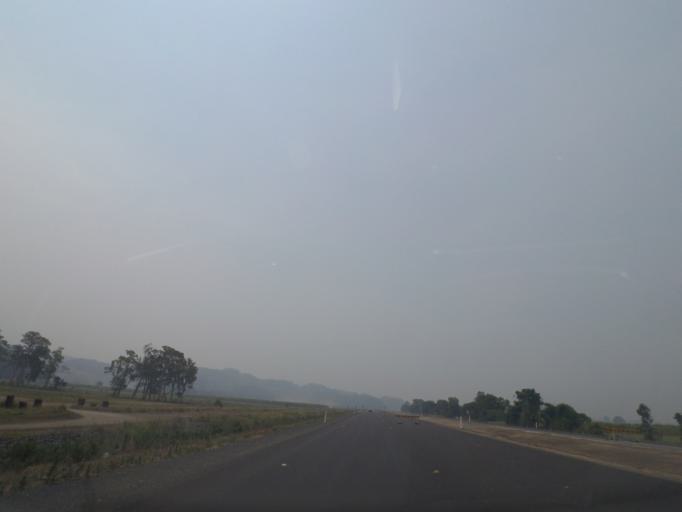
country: AU
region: New South Wales
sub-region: Ballina
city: Ballina
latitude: -28.8927
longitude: 153.4816
